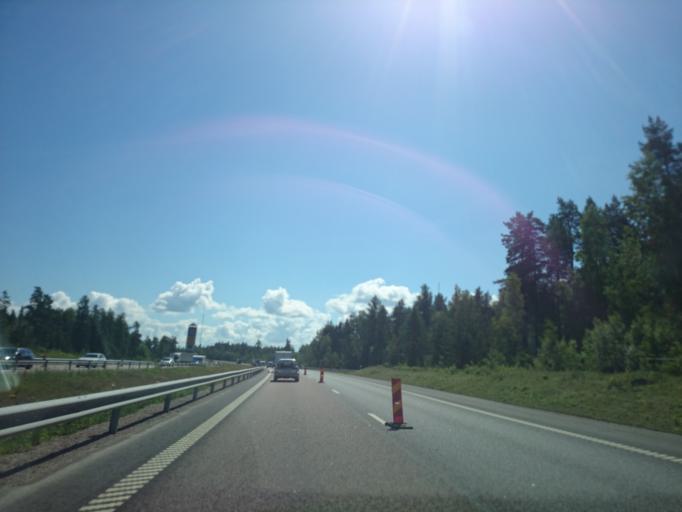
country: SE
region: Gaevleborg
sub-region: Gavle Kommun
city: Gavle
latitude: 60.6482
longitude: 17.1195
